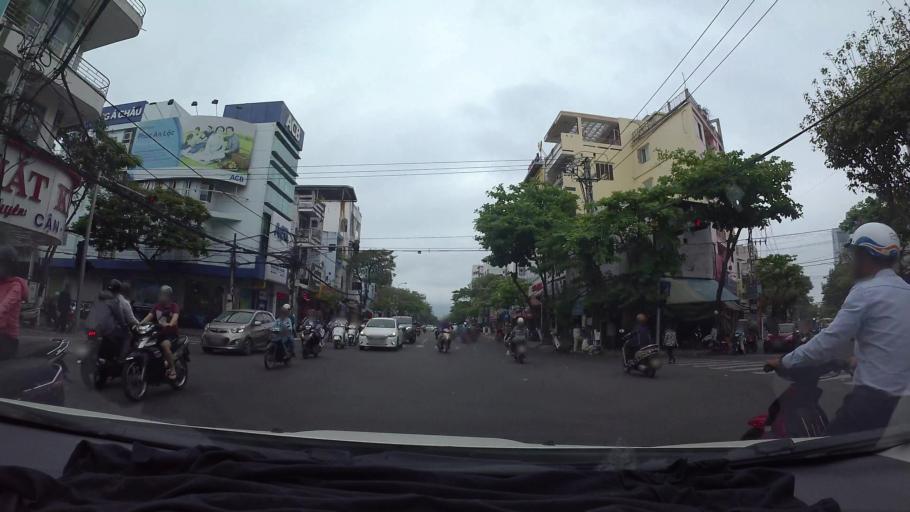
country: VN
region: Da Nang
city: Da Nang
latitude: 16.0768
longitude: 108.2161
